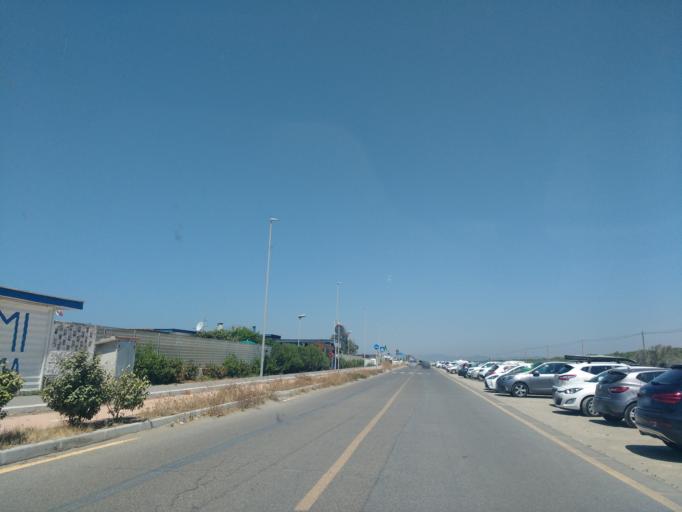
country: IT
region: Latium
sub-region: Citta metropolitana di Roma Capitale
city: Passo Oscuro
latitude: 41.8788
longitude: 12.1757
